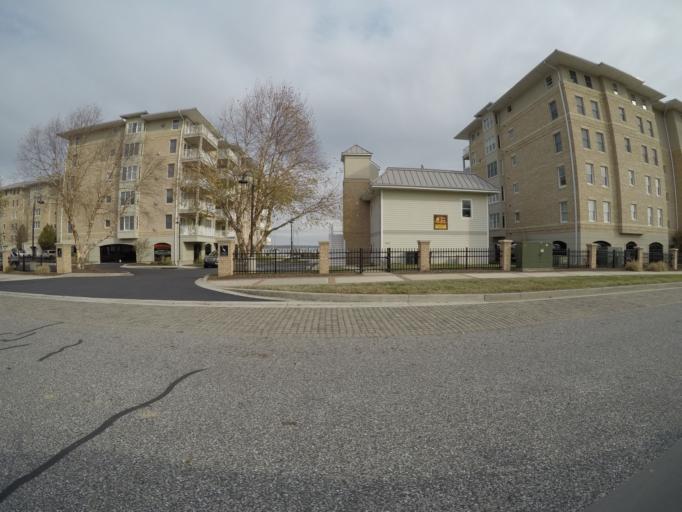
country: US
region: Maryland
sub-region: Harford County
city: Havre de Grace
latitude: 39.5424
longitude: -76.0853
